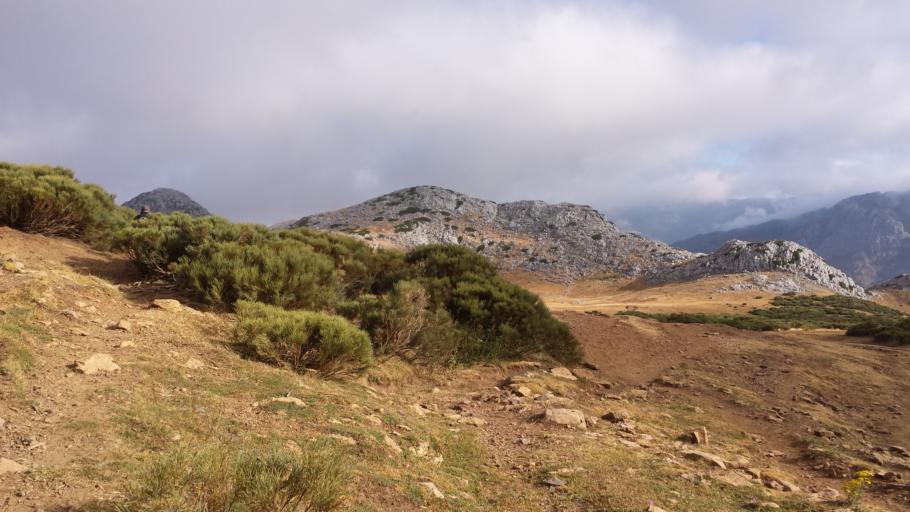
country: ES
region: Castille and Leon
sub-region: Provincia de Leon
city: Vegacervera
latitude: 42.9246
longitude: -5.4696
